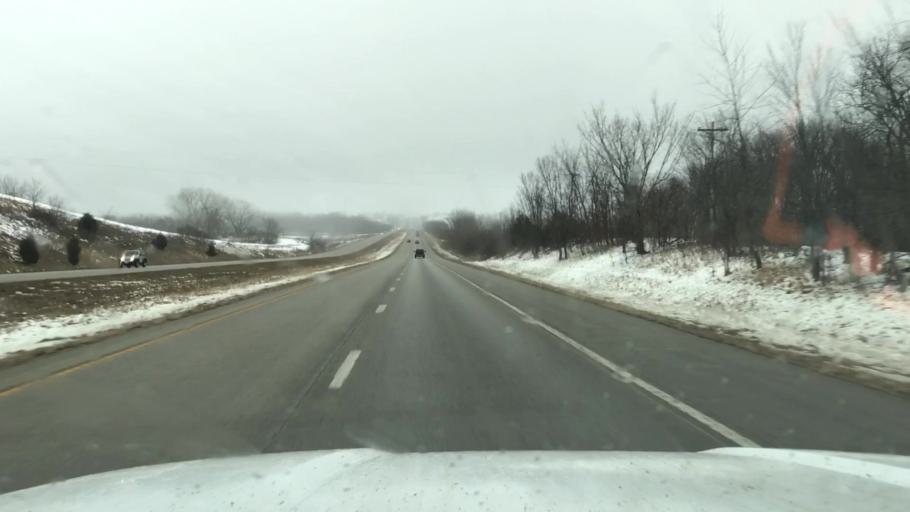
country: US
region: Missouri
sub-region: Clinton County
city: Gower
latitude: 39.7474
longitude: -94.6747
